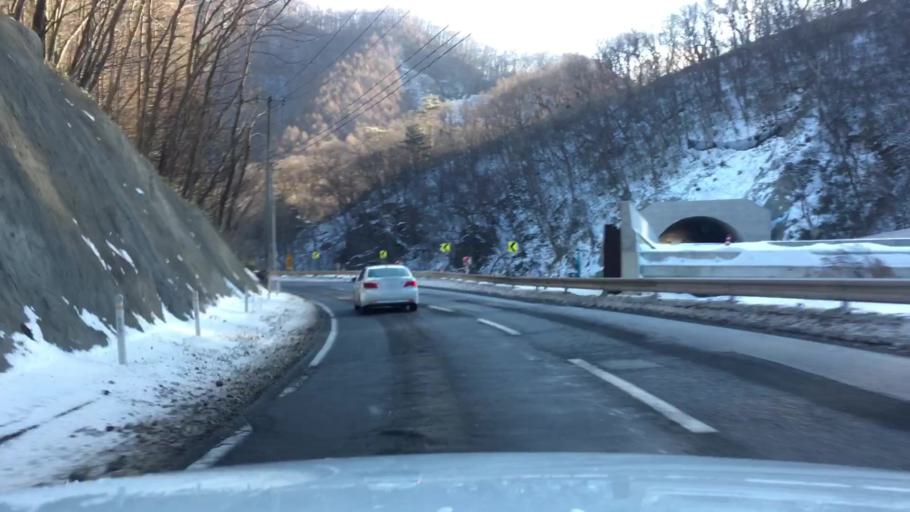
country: JP
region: Iwate
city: Morioka-shi
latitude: 39.6314
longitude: 141.4570
